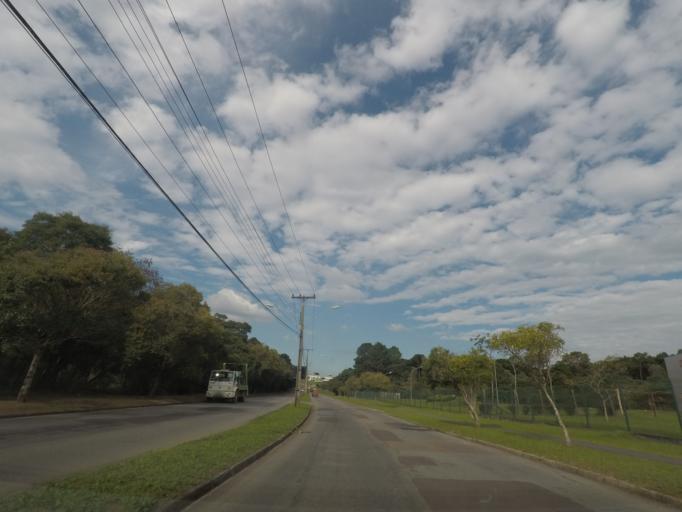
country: BR
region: Parana
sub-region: Sao Jose Dos Pinhais
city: Sao Jose dos Pinhais
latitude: -25.5343
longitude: -49.3064
